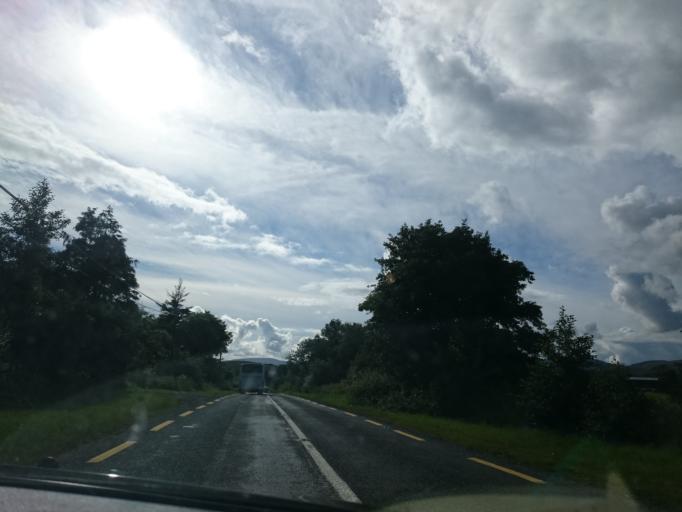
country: IE
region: Connaught
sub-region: Maigh Eo
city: Westport
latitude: 53.9015
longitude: -9.6102
